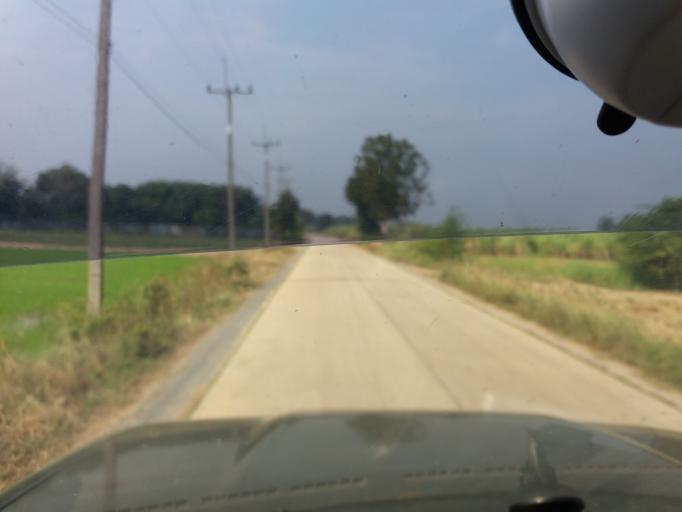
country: TH
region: Suphan Buri
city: Doem Bang Nang Buat
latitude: 14.8934
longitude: 100.1959
